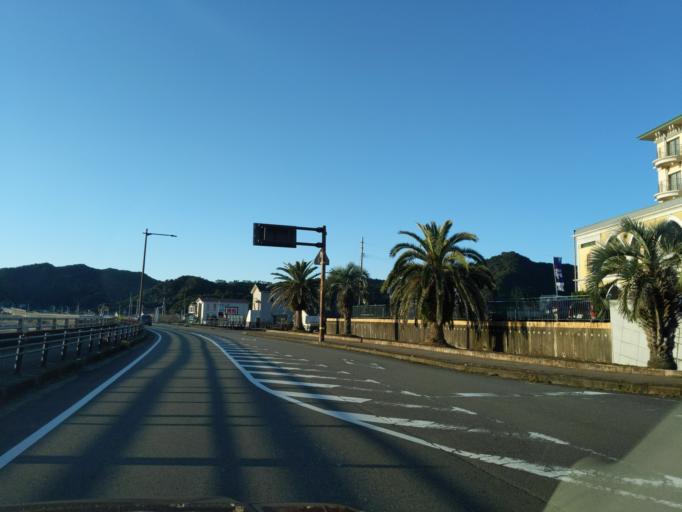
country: JP
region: Kochi
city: Muroto-misakicho
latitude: 33.5686
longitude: 134.3077
